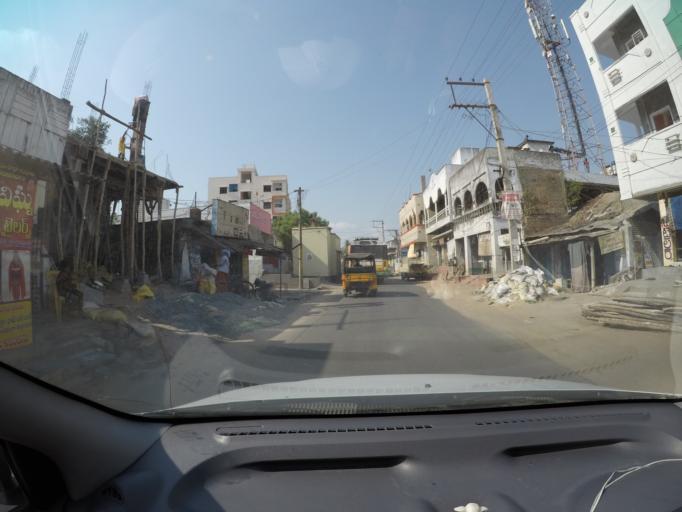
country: IN
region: Andhra Pradesh
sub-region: Krishna
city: Kankipadu
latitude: 16.4354
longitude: 80.7685
